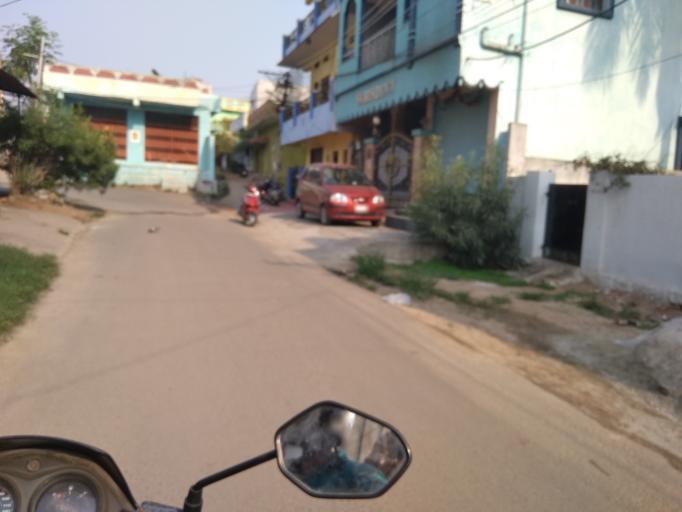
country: IN
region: Telangana
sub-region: Hyderabad
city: Malkajgiri
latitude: 17.4605
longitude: 78.5554
